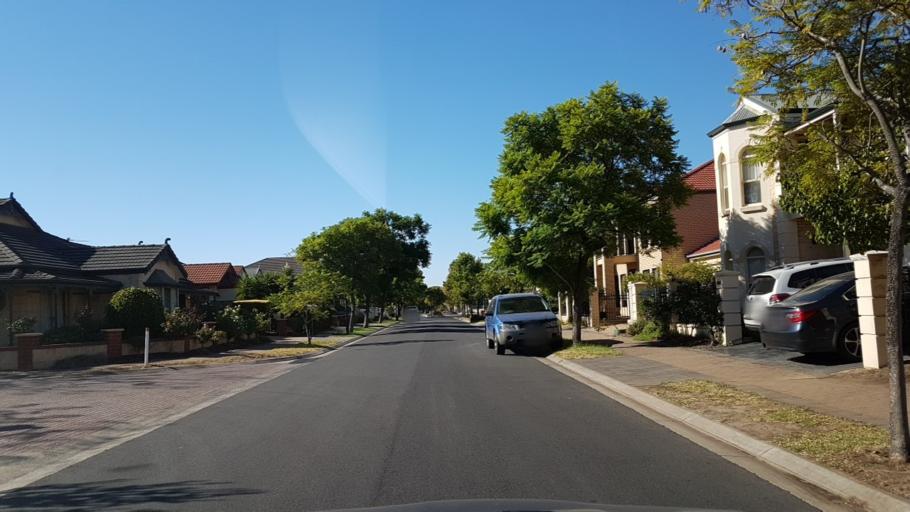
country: AU
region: South Australia
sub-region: Salisbury
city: Ingle Farm
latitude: -34.8126
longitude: 138.6109
